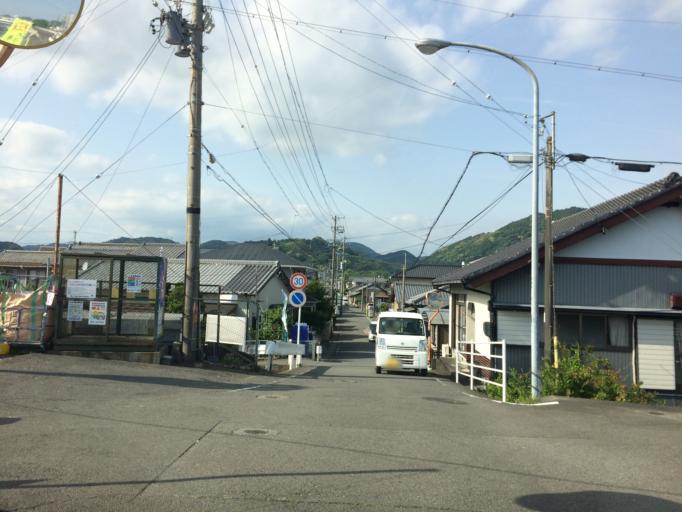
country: JP
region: Shizuoka
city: Fujieda
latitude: 34.8984
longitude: 138.2838
